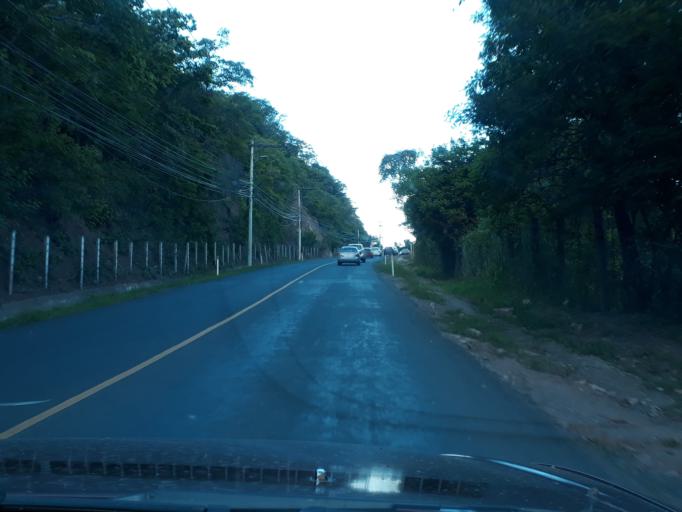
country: HN
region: Francisco Morazan
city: Santa Lucia
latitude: 14.1108
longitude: -87.1634
